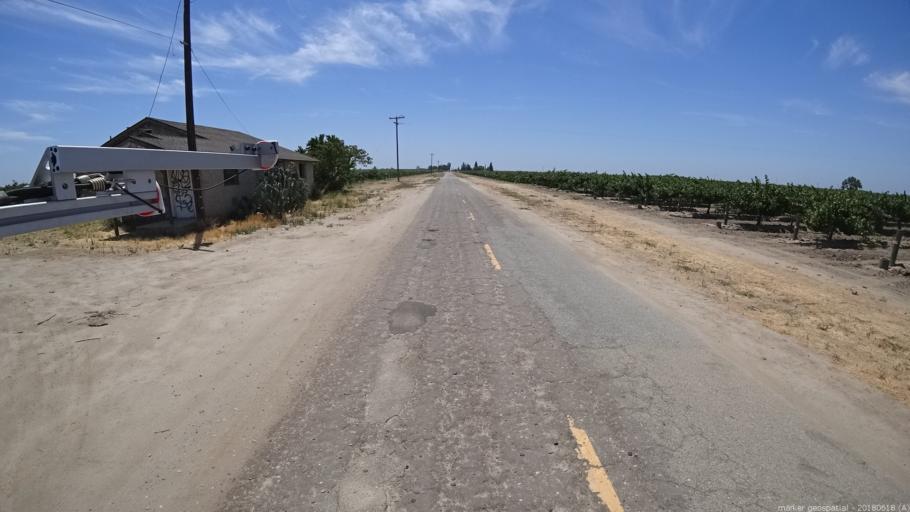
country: US
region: California
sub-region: Madera County
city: Parkwood
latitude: 36.8988
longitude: -120.1196
